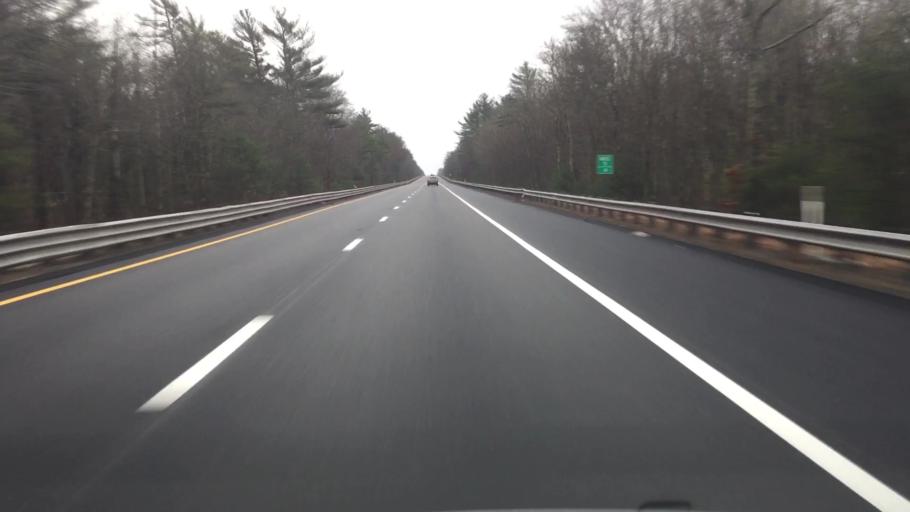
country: US
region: Massachusetts
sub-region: Plymouth County
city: West Wareham
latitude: 41.8296
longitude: -70.8150
